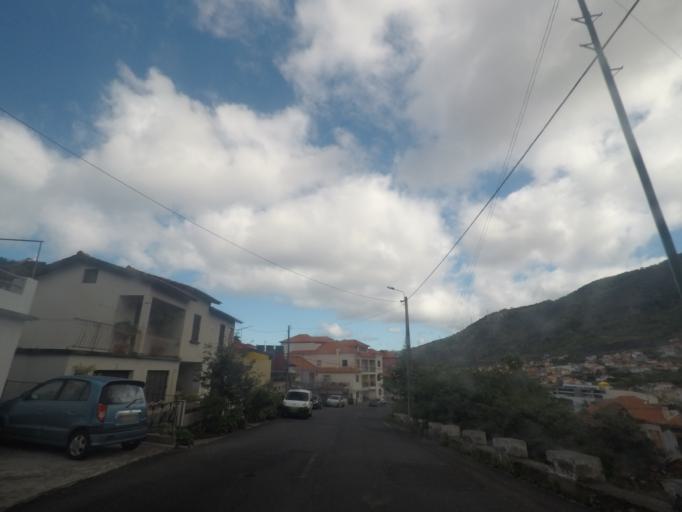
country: PT
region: Madeira
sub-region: Machico
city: Machico
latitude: 32.7286
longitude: -16.7711
